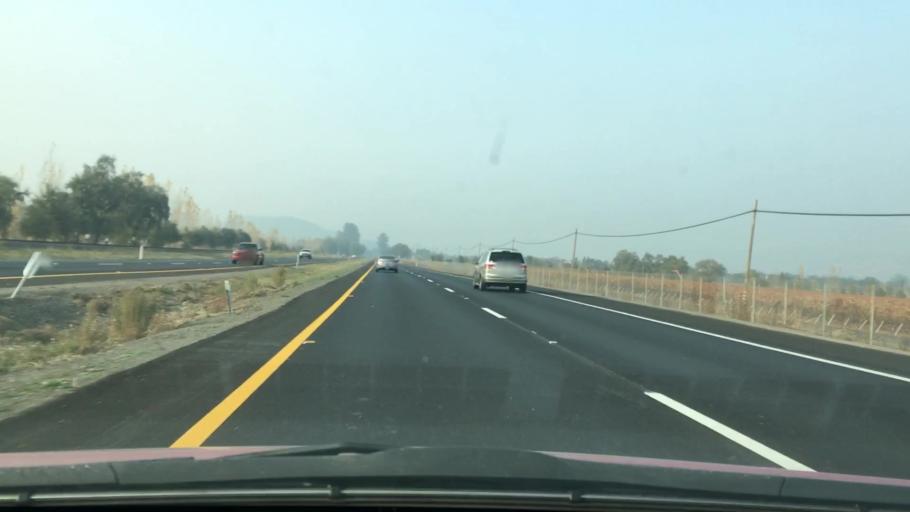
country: US
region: California
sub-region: Napa County
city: Yountville
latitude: 38.3789
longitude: -122.3449
